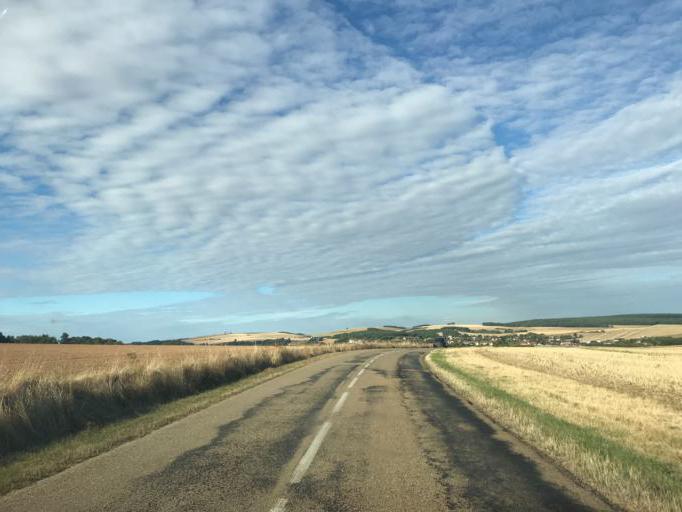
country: FR
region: Bourgogne
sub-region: Departement de l'Yonne
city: Fontenailles
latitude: 47.6028
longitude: 3.4830
